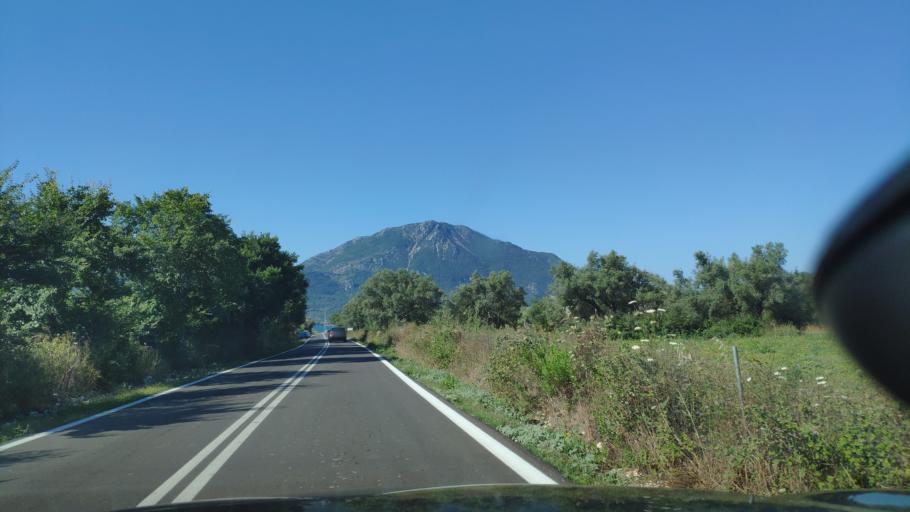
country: GR
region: West Greece
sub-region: Nomos Aitolias kai Akarnanias
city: Kandila
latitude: 38.6797
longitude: 20.9416
